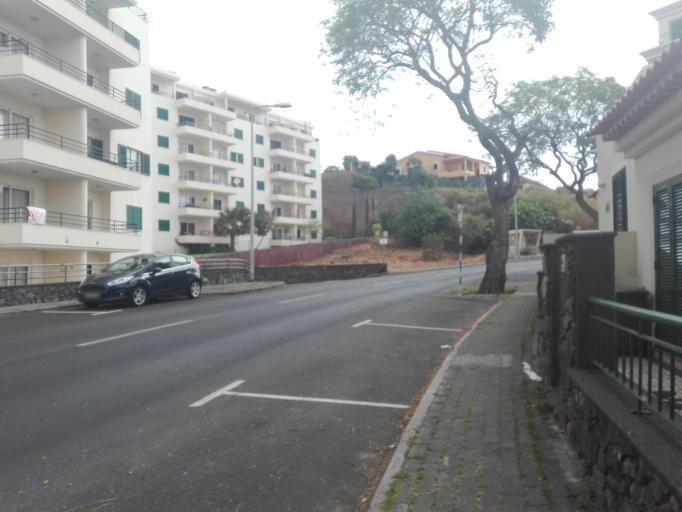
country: PT
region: Madeira
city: Canico
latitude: 32.6492
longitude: -16.8265
